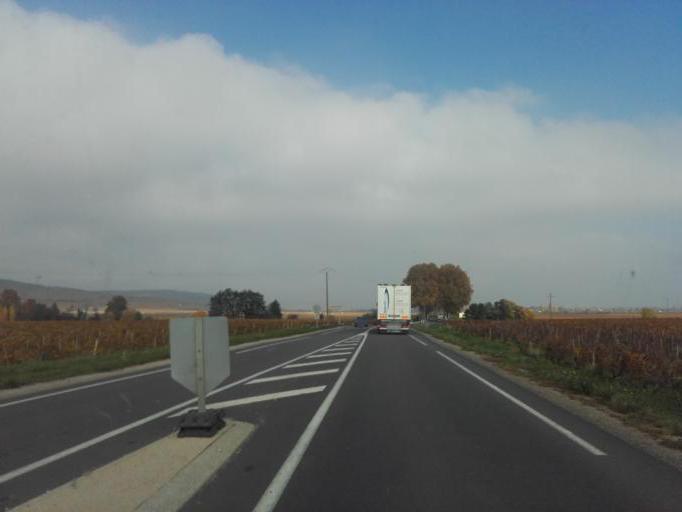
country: FR
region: Bourgogne
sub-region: Departement de la Cote-d'Or
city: Bligny-les-Beaune
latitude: 47.0026
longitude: 4.8011
